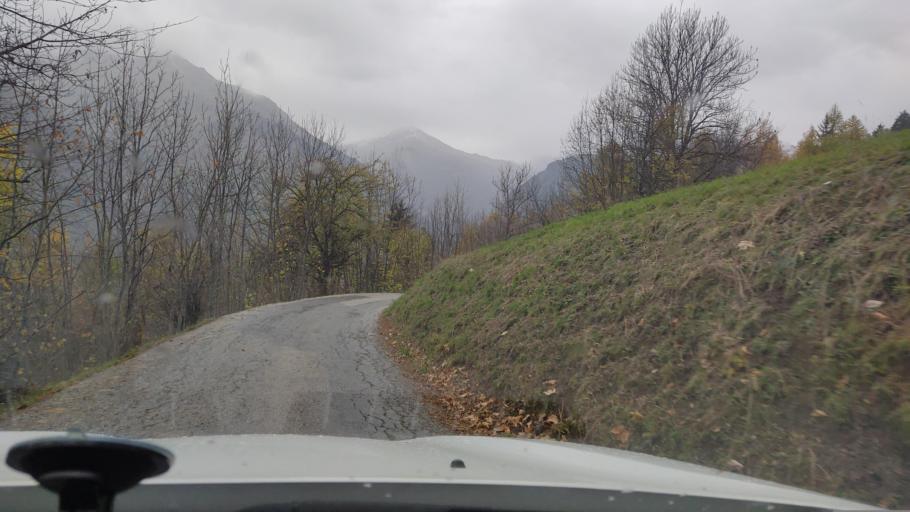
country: FR
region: Rhone-Alpes
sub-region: Departement de la Savoie
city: Bourg-Saint-Maurice
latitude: 45.5997
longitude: 6.7745
